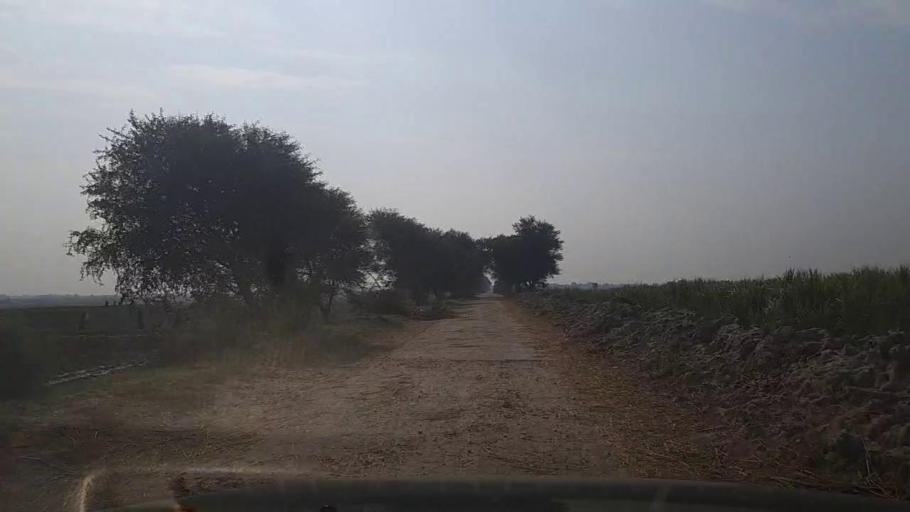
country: PK
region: Sindh
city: Bulri
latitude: 25.0210
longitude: 68.2993
